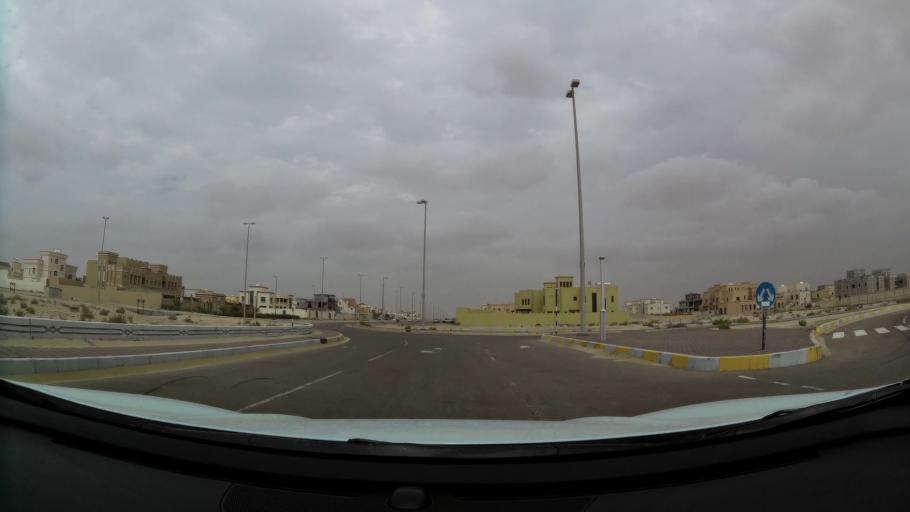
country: AE
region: Abu Dhabi
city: Abu Dhabi
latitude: 24.3934
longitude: 54.6519
